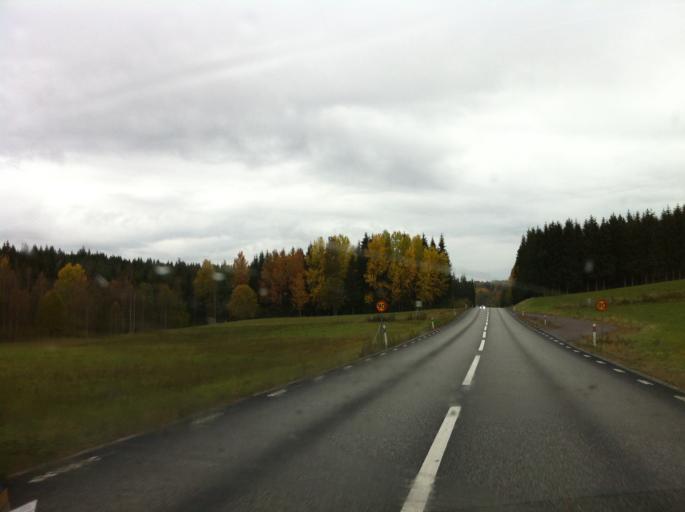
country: SE
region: OErebro
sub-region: Lindesbergs Kommun
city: Stora
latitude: 59.6719
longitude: 15.1006
